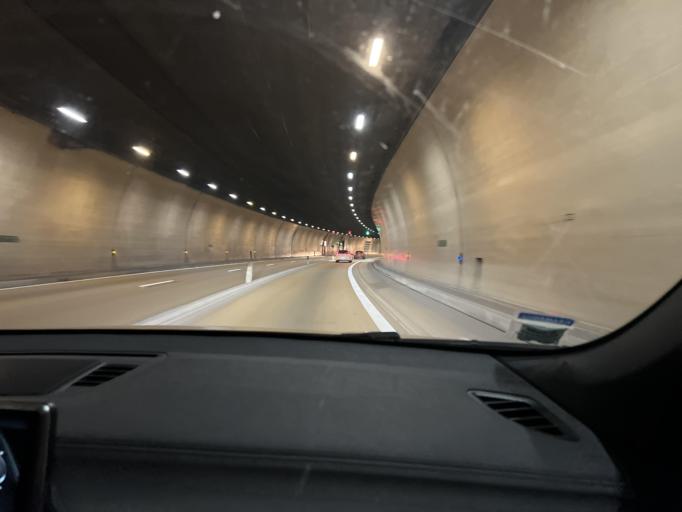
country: FR
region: Provence-Alpes-Cote d'Azur
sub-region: Departement des Alpes-Maritimes
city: La Turbie
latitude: 43.7449
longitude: 7.3827
